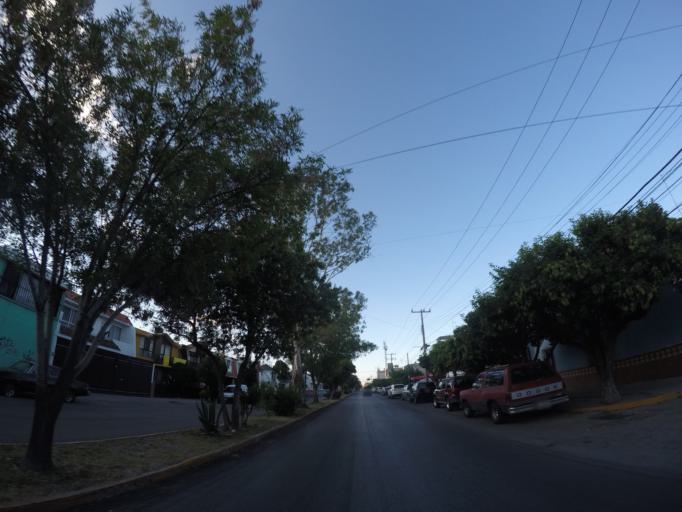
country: MX
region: San Luis Potosi
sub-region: San Luis Potosi
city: San Luis Potosi
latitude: 22.1370
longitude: -100.9882
